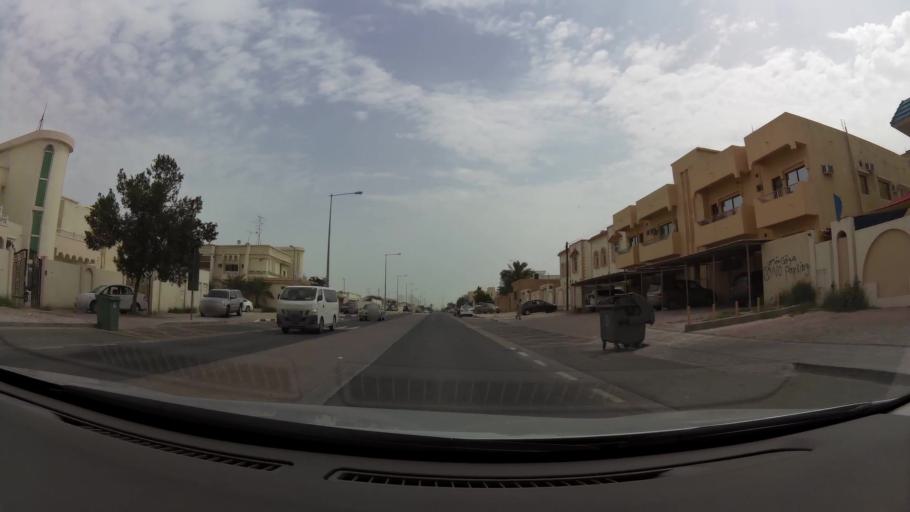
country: QA
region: Baladiyat ar Rayyan
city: Ar Rayyan
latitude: 25.3104
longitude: 51.4749
